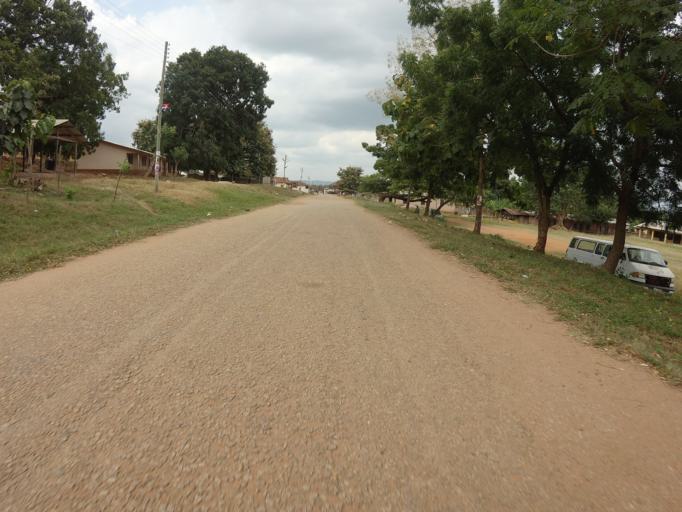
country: GH
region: Volta
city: Ho
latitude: 6.6481
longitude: 0.3389
